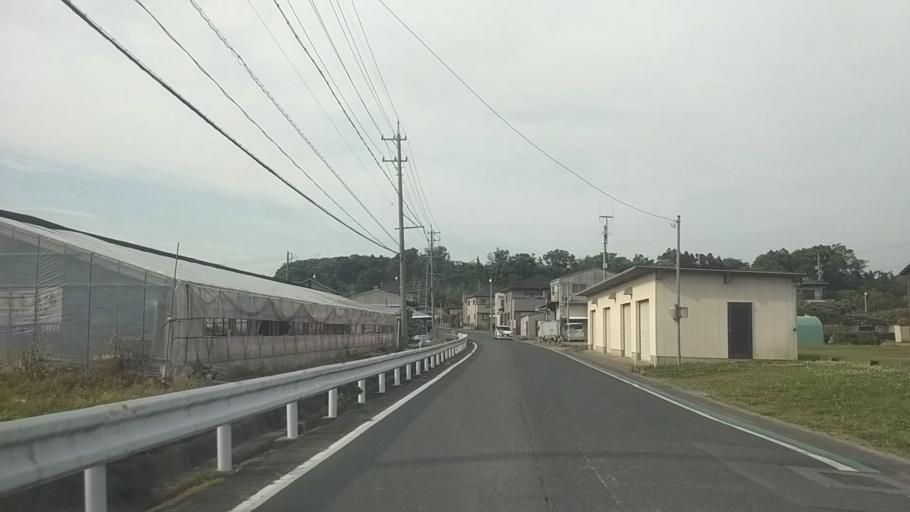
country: JP
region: Shizuoka
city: Kosai-shi
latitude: 34.7426
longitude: 137.6142
